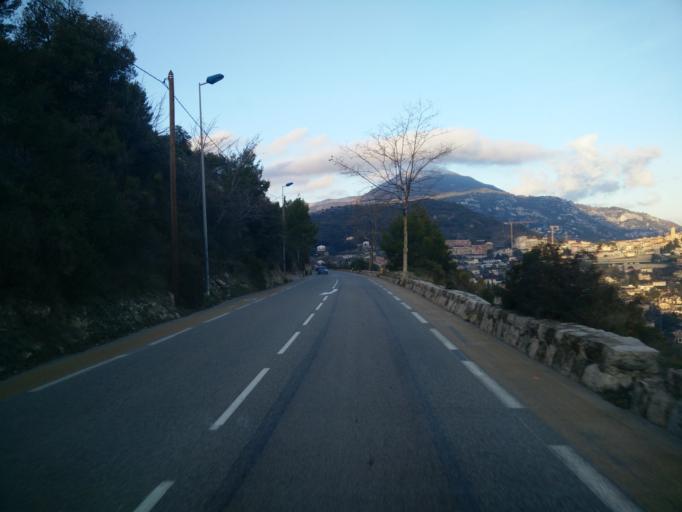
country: FR
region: Provence-Alpes-Cote d'Azur
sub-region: Departement des Alpes-Maritimes
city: La Turbie
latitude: 43.7393
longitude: 7.3897
